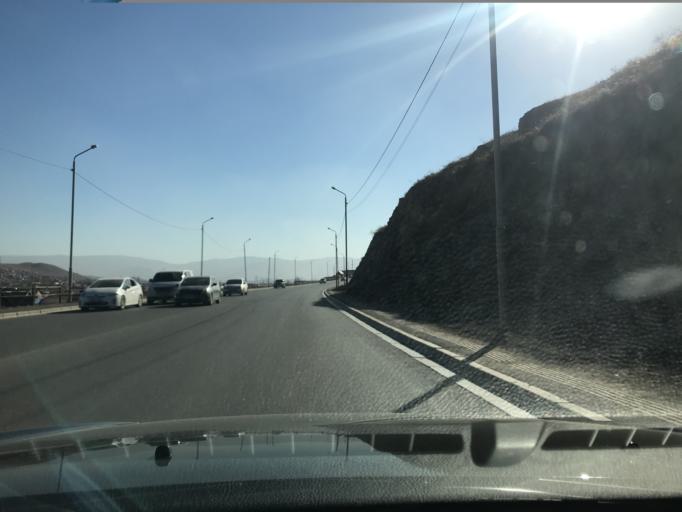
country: MN
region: Ulaanbaatar
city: Ulaanbaatar
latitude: 47.9869
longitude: 106.9250
